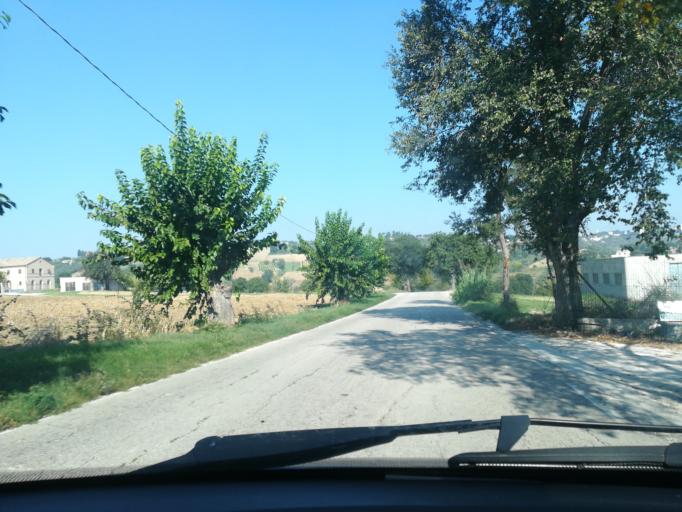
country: IT
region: The Marches
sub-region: Provincia di Macerata
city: Macerata
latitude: 43.2698
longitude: 13.4510
